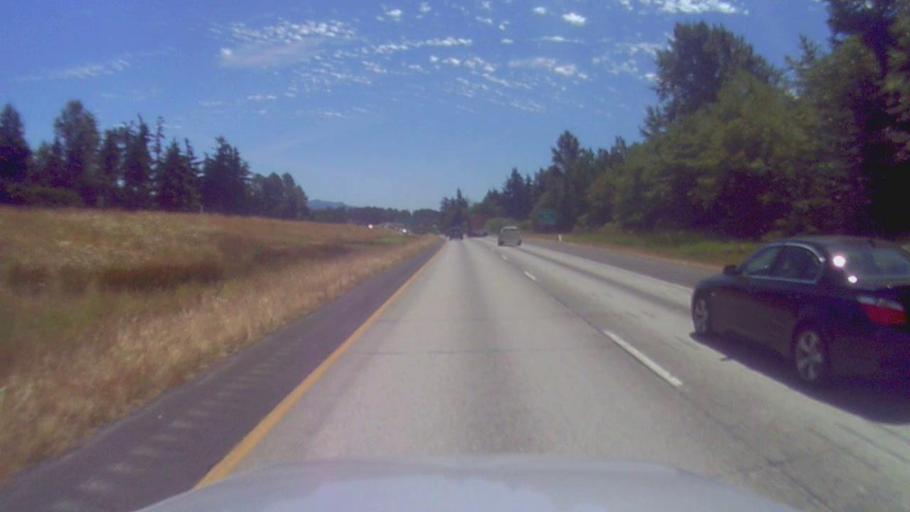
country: US
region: Washington
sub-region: Whatcom County
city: Marietta-Alderwood
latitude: 48.7946
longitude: -122.5265
